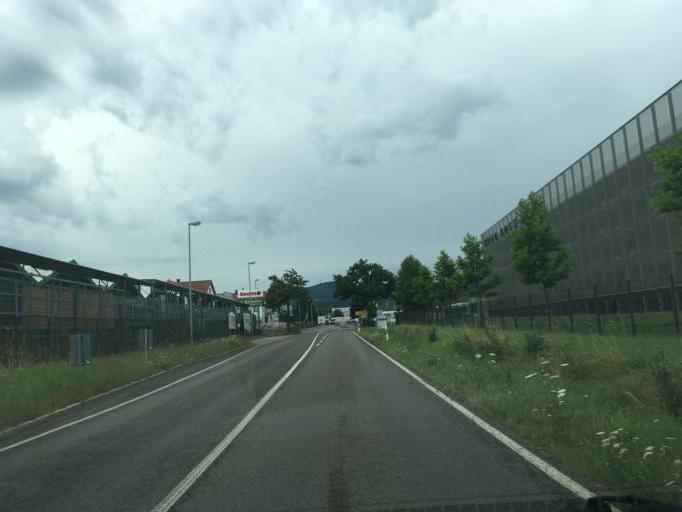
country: DE
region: Baden-Wuerttemberg
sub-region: Tuebingen Region
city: Metzingen
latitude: 48.5452
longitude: 9.2733
